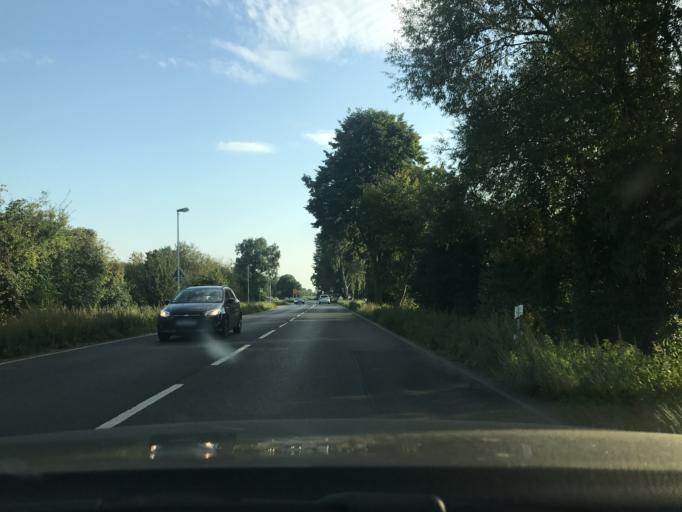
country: DE
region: North Rhine-Westphalia
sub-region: Regierungsbezirk Dusseldorf
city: Rheurdt
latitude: 51.3989
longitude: 6.4976
